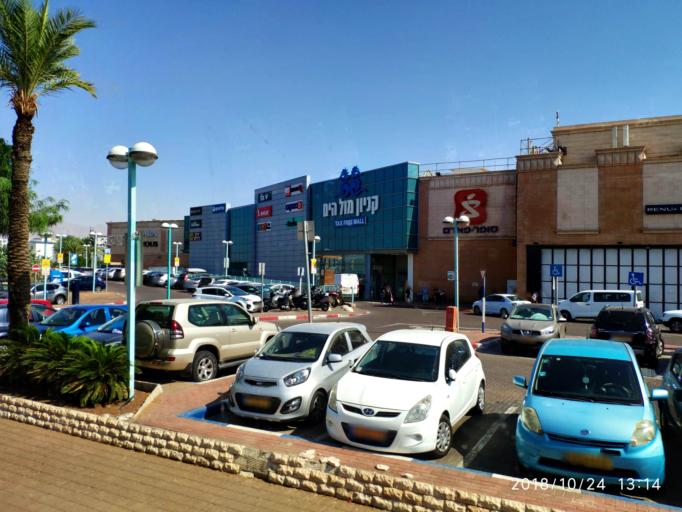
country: IL
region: Southern District
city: Eilat
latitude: 29.5498
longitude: 34.9530
